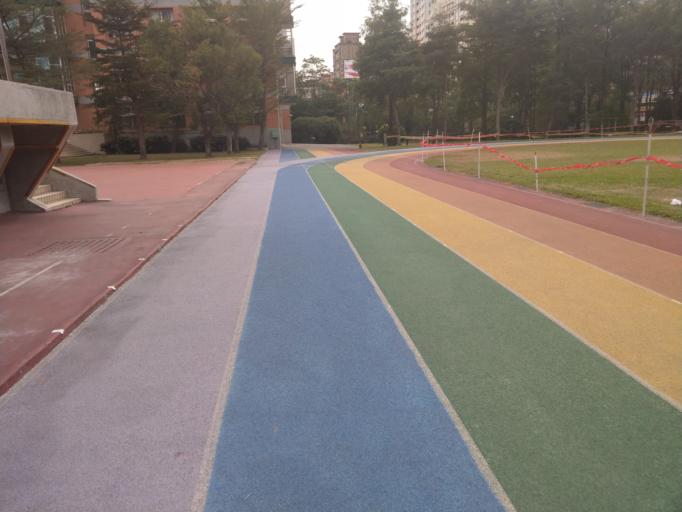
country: TW
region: Taiwan
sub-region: Taichung City
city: Taichung
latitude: 24.1528
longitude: 120.6378
